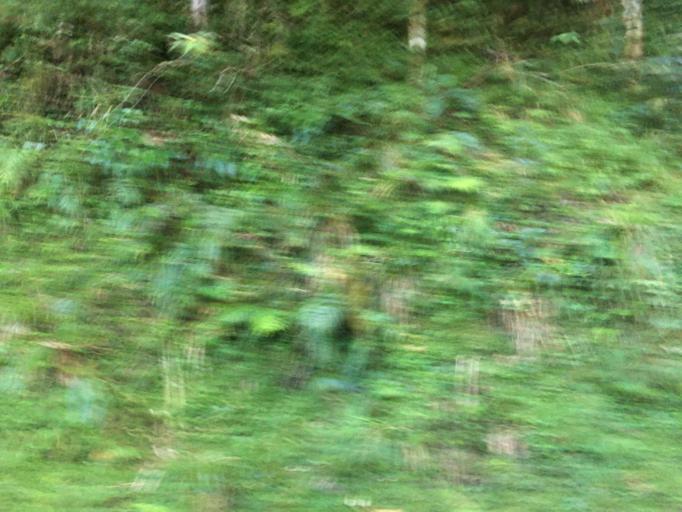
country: TW
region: Taiwan
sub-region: Yilan
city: Yilan
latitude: 24.6197
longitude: 121.4810
